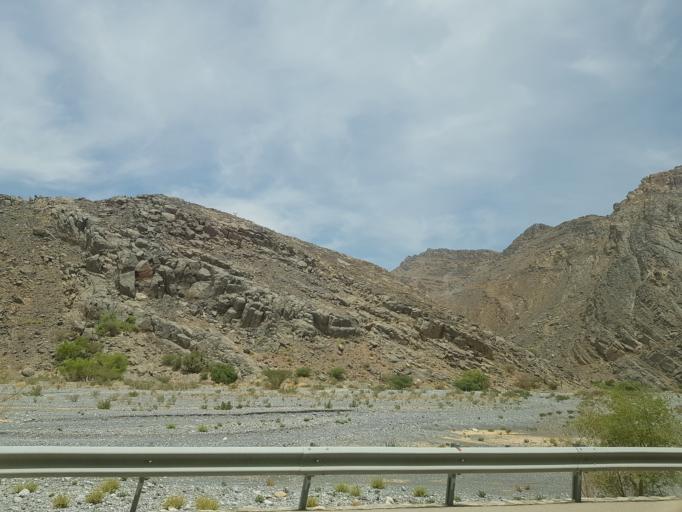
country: OM
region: Muhafazat ad Dakhiliyah
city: Izki
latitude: 22.9348
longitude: 57.6734
